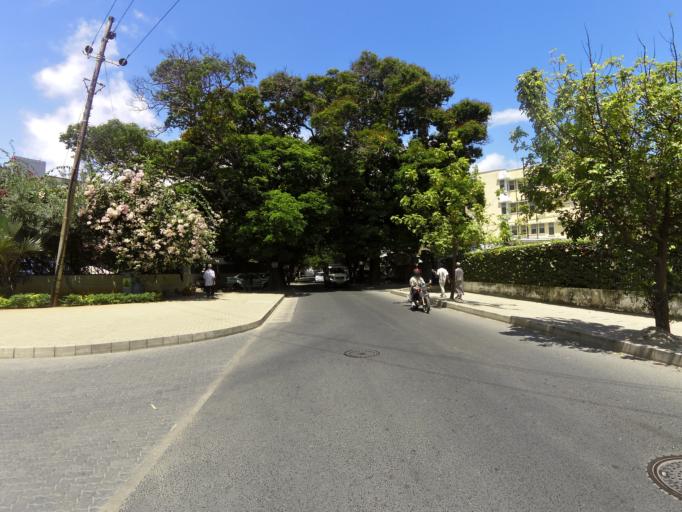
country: TZ
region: Dar es Salaam
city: Dar es Salaam
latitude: -6.8152
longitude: 39.2933
